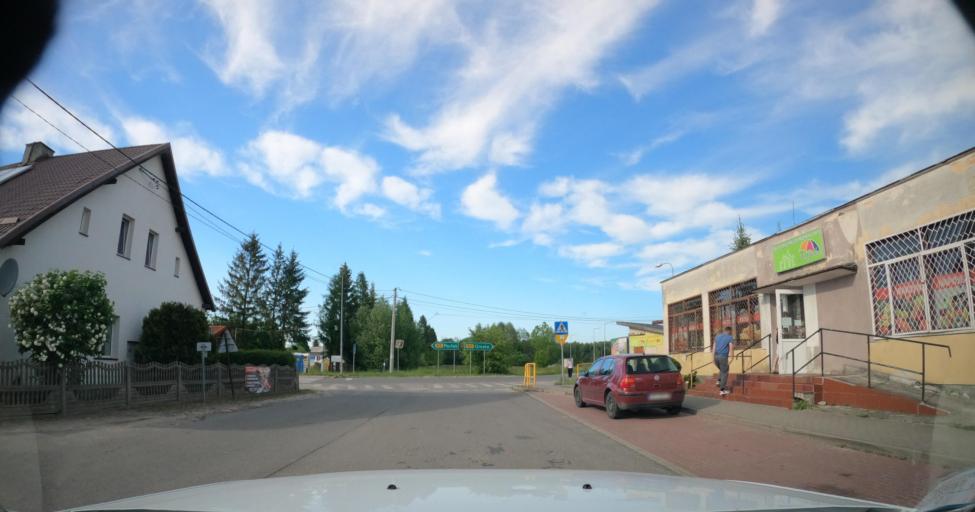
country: PL
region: Warmian-Masurian Voivodeship
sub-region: Powiat ostrodzki
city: Morag
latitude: 54.0796
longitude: 19.9036
